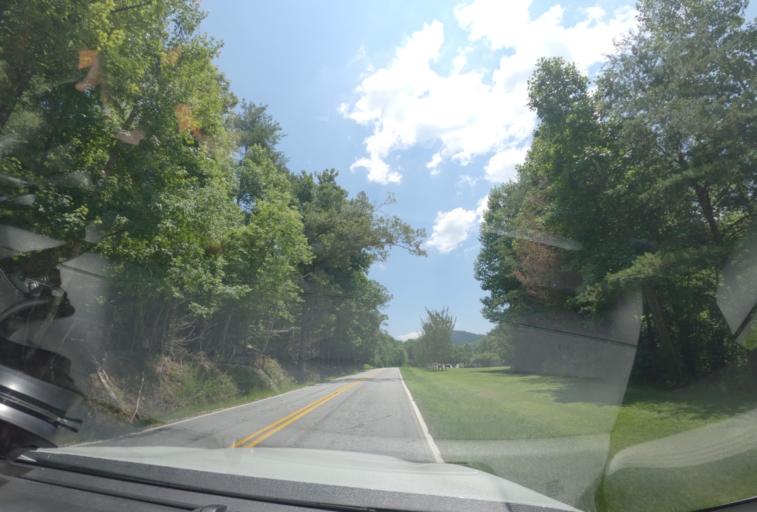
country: US
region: South Carolina
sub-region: Pickens County
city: Pickens
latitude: 34.9863
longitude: -82.8505
